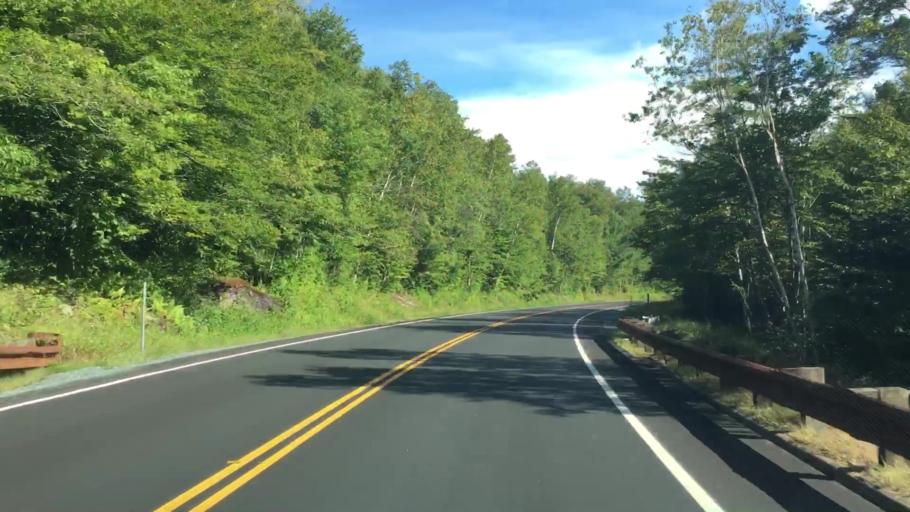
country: US
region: New Hampshire
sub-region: Grafton County
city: Woodstock
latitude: 44.0261
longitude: -71.7543
